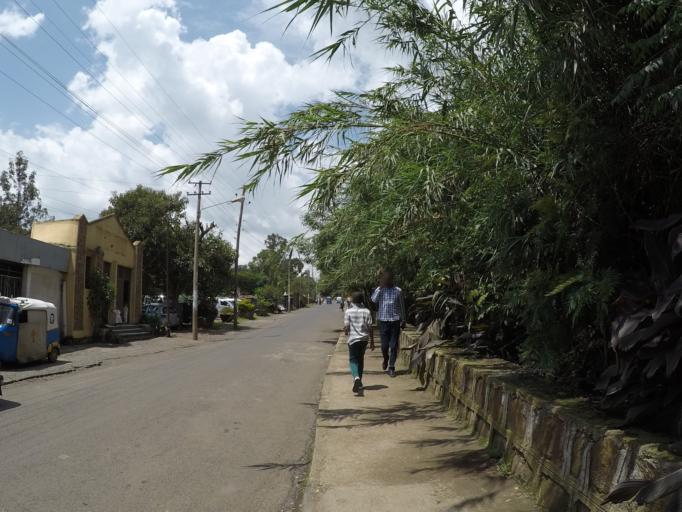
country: ET
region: Amhara
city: Gondar
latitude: 12.6107
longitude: 37.4707
